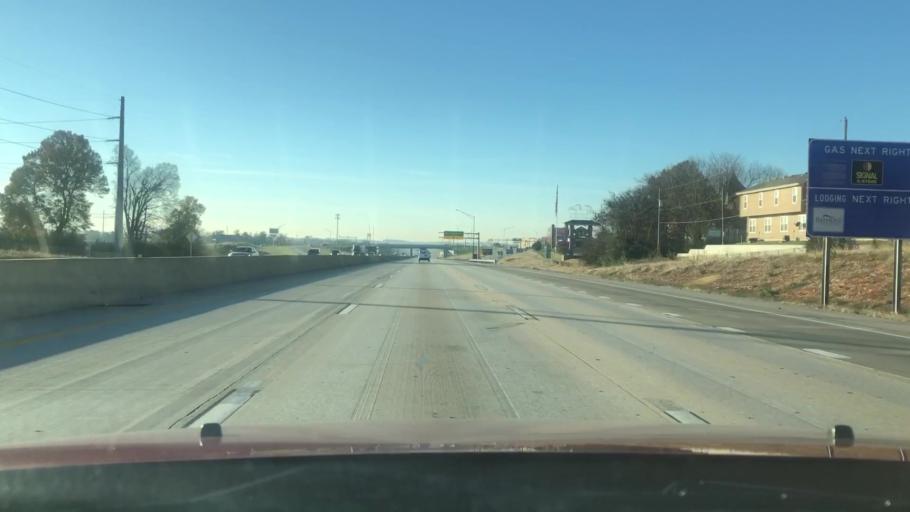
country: US
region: Missouri
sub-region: Greene County
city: Springfield
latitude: 37.1628
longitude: -93.2245
